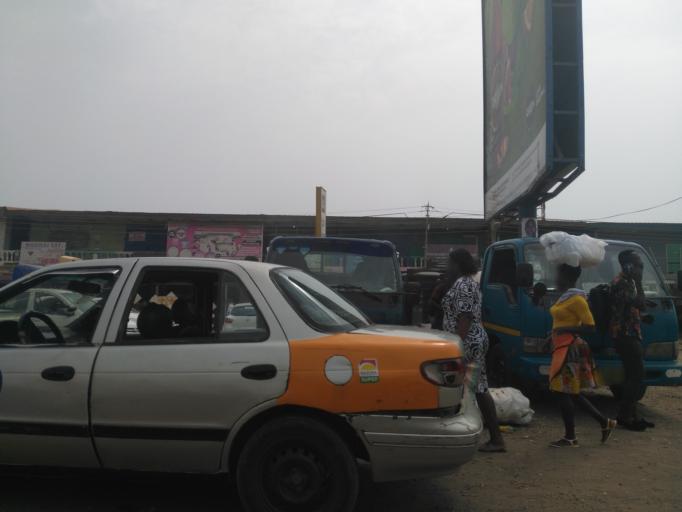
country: GH
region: Greater Accra
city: Nungua
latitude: 5.6006
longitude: -0.0801
